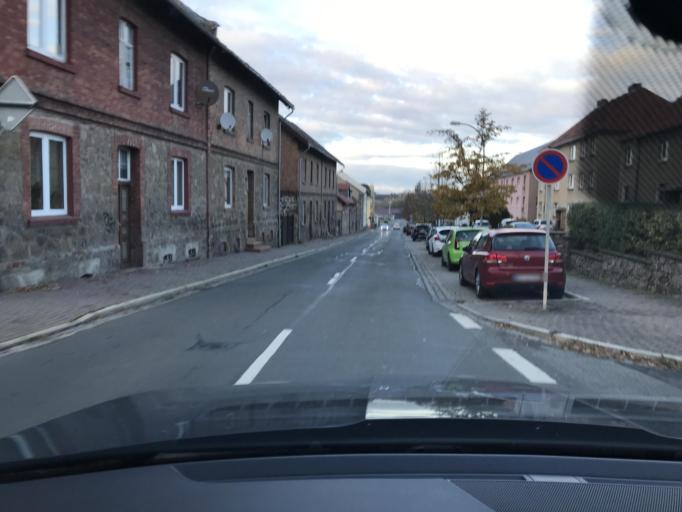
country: DE
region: Saxony-Anhalt
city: Thale
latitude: 51.7479
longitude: 11.0398
